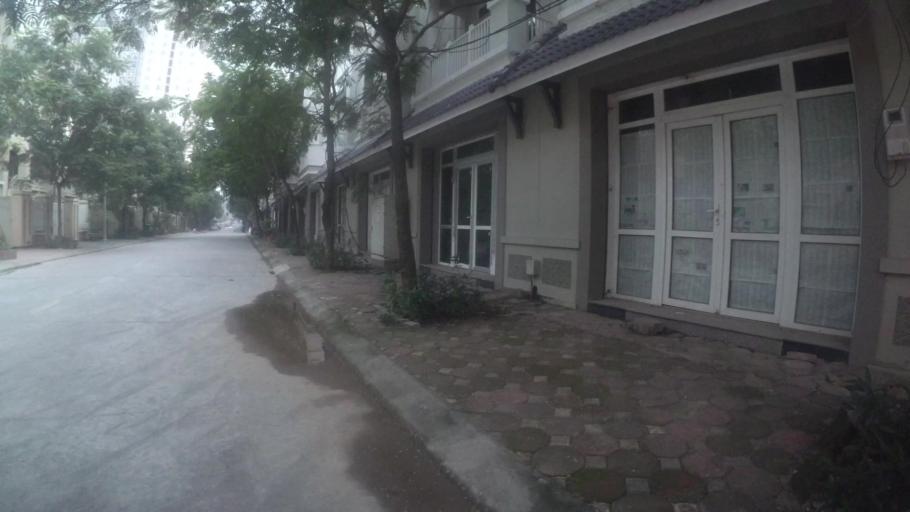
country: VN
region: Ha Noi
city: Cau Dien
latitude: 21.0046
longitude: 105.7310
